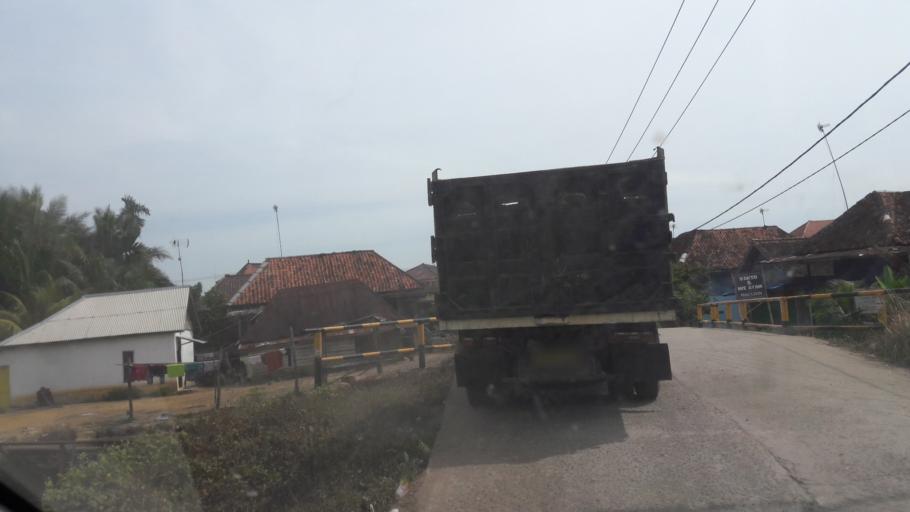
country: ID
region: South Sumatra
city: Gunungmenang
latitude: -3.2543
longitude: 104.1464
